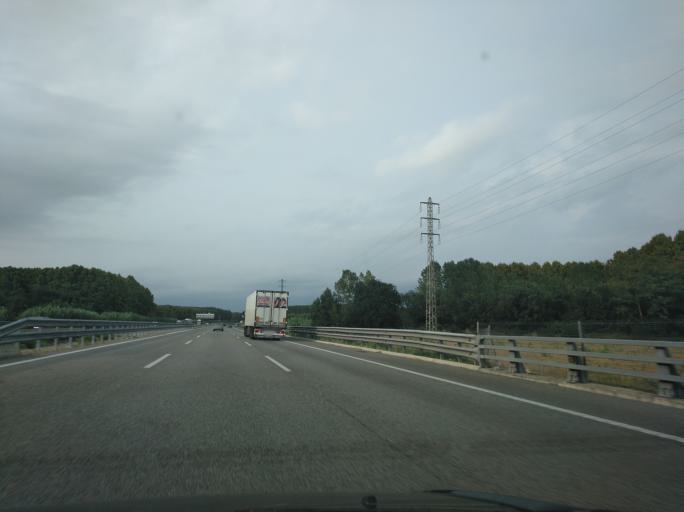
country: ES
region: Catalonia
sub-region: Provincia de Girona
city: Sils
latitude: 41.7932
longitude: 2.7462
